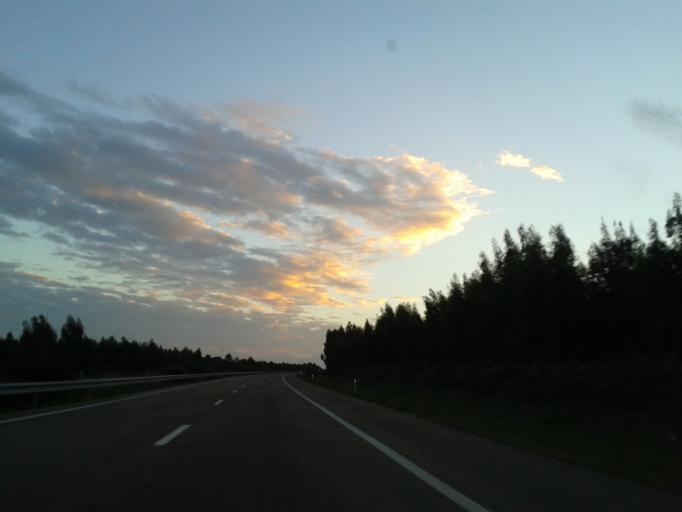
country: PT
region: Evora
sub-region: Vendas Novas
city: Vendas Novas
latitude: 38.6751
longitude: -8.6435
